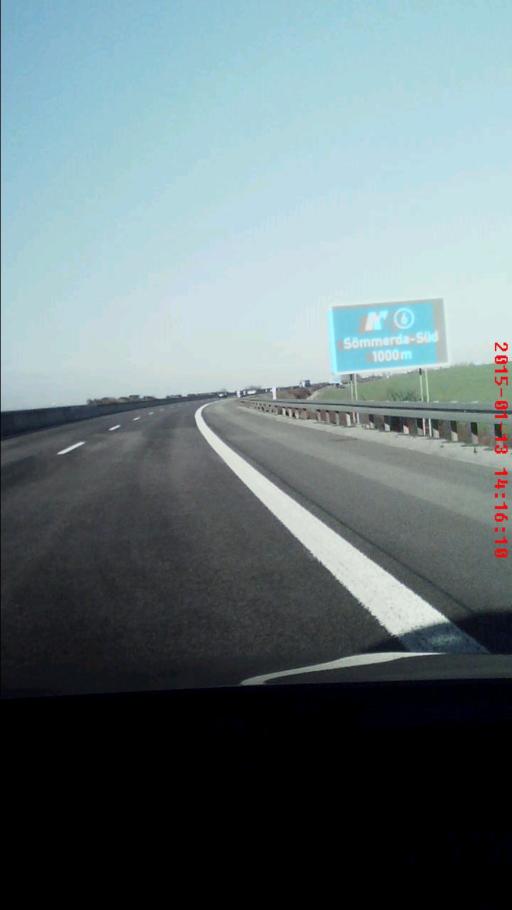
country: DE
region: Thuringia
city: Schlossvippach
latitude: 51.1043
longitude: 11.1256
